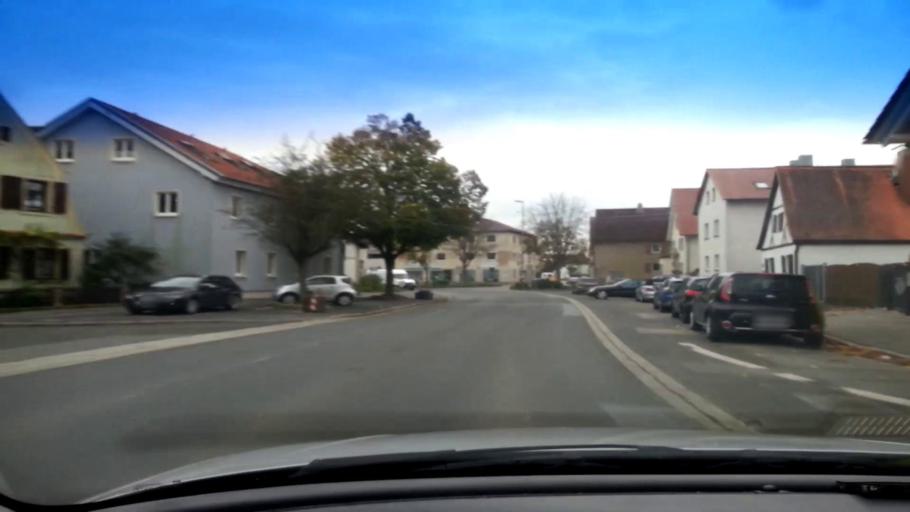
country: DE
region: Bavaria
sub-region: Upper Franconia
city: Hallstadt
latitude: 49.9297
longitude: 10.8694
